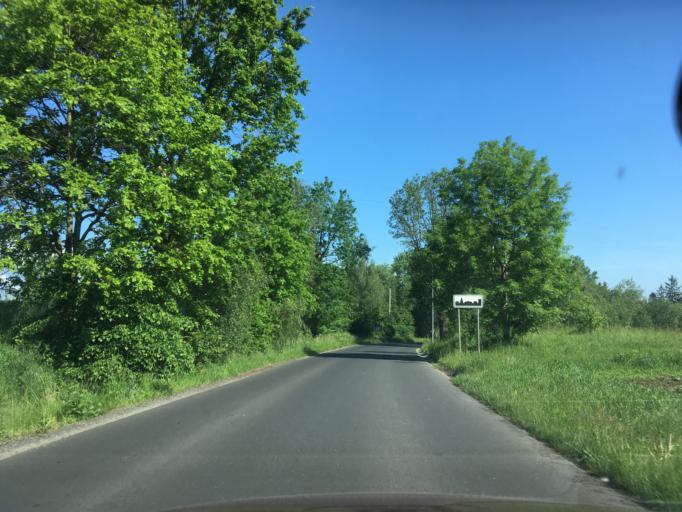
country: PL
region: Lower Silesian Voivodeship
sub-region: Powiat zgorzelecki
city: Sulikow
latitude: 51.1090
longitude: 15.0337
